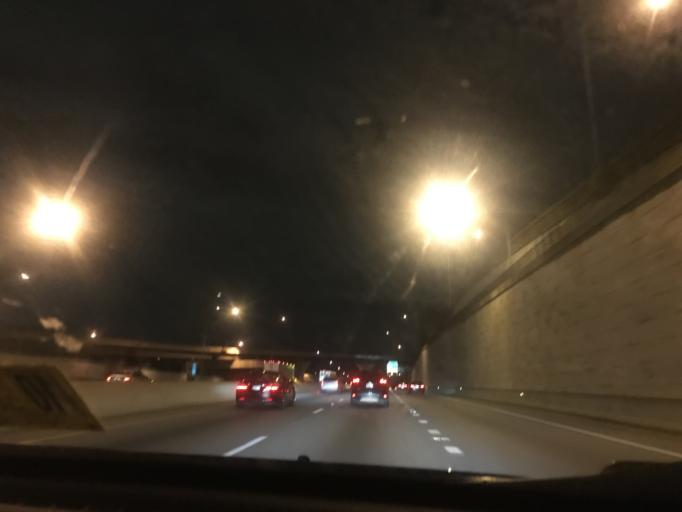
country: US
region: Maryland
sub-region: Prince George's County
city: Forest Heights
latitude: 38.7998
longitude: -77.0047
